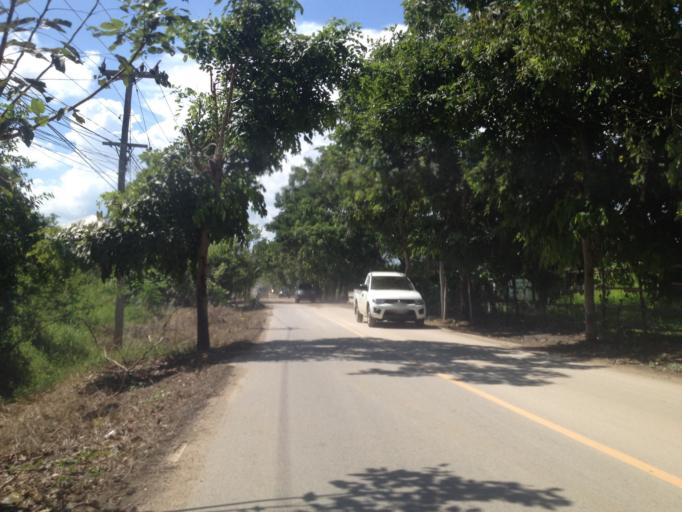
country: TH
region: Chiang Mai
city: Hang Dong
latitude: 18.6828
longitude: 98.9767
